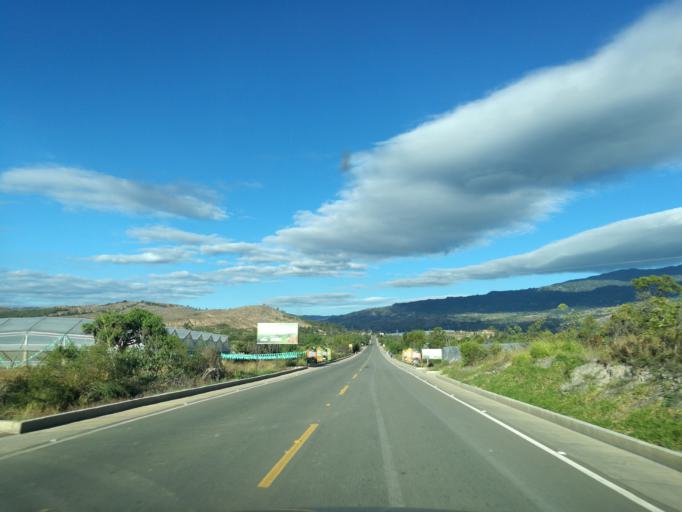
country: CO
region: Boyaca
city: Sutamarchan
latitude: 5.6251
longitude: -73.5907
